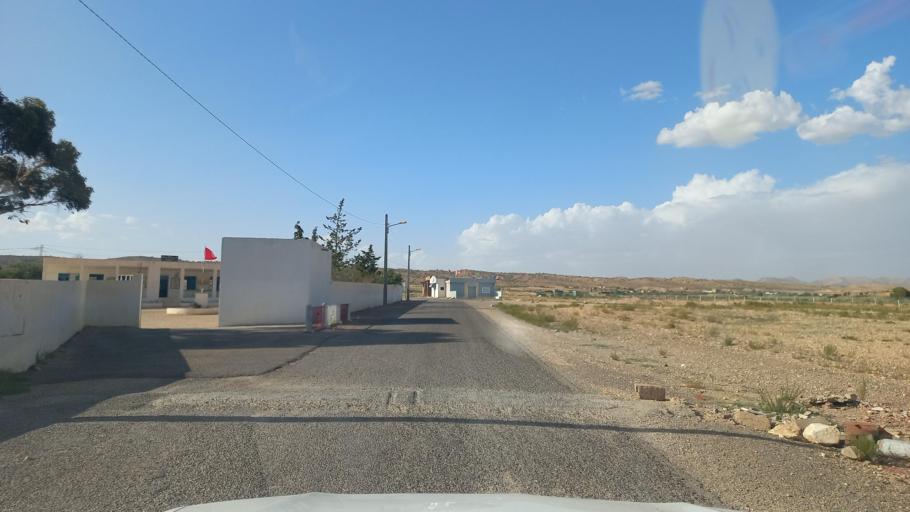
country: TN
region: Al Qasrayn
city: Sbiba
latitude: 35.3437
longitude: 8.9908
